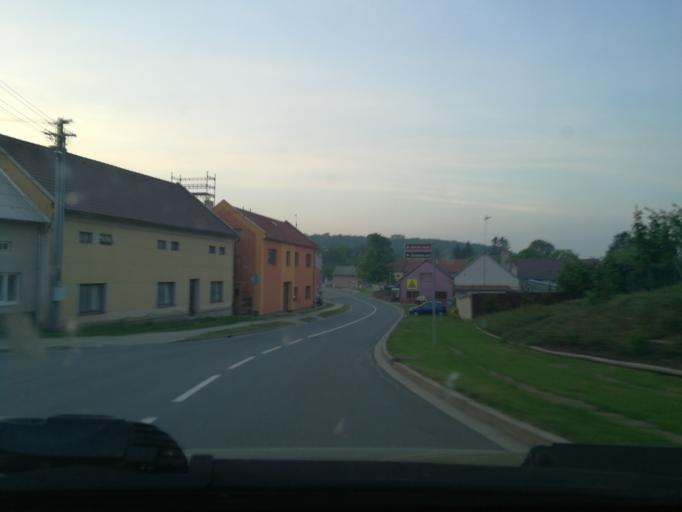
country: CZ
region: Zlin
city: Tlumacov
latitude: 49.2755
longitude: 17.5488
